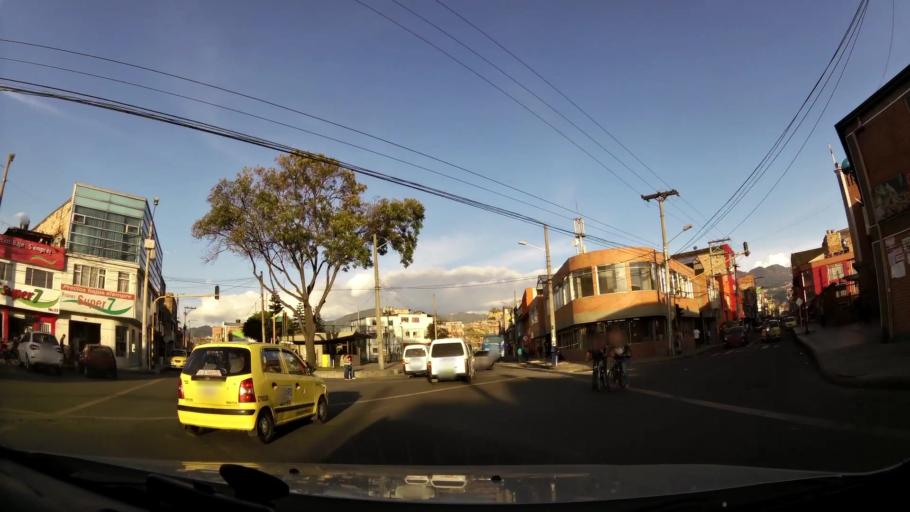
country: CO
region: Bogota D.C.
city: Bogota
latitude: 4.5673
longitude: -74.1301
